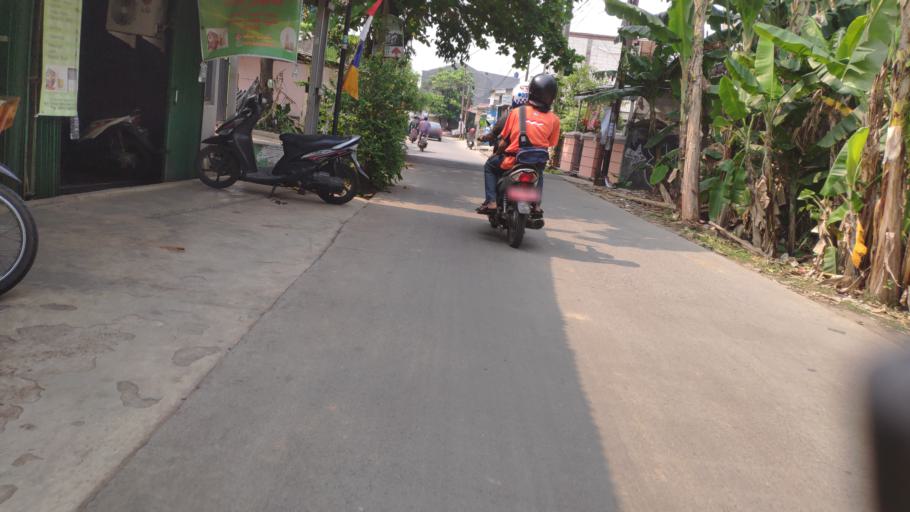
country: ID
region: West Java
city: Depok
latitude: -6.3837
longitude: 106.8043
